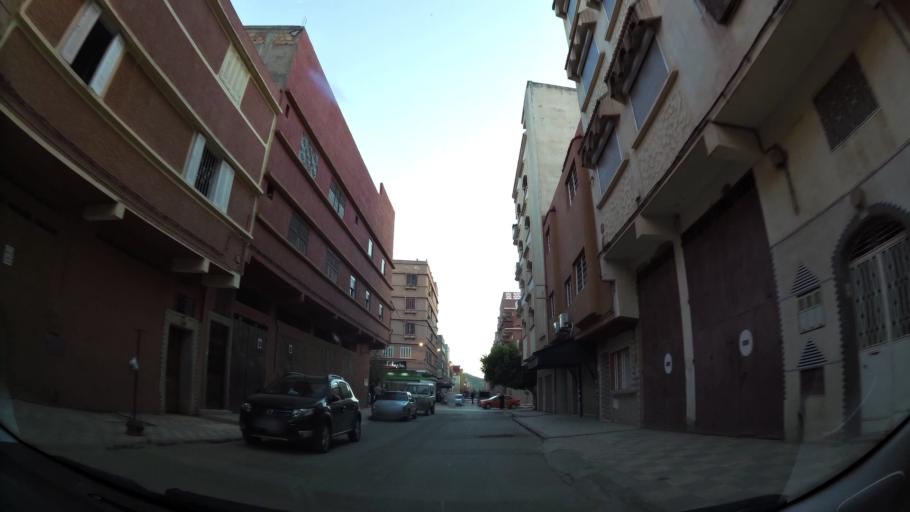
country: MA
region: Oriental
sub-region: Berkane-Taourirt
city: Berkane
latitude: 34.9200
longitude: -2.3204
